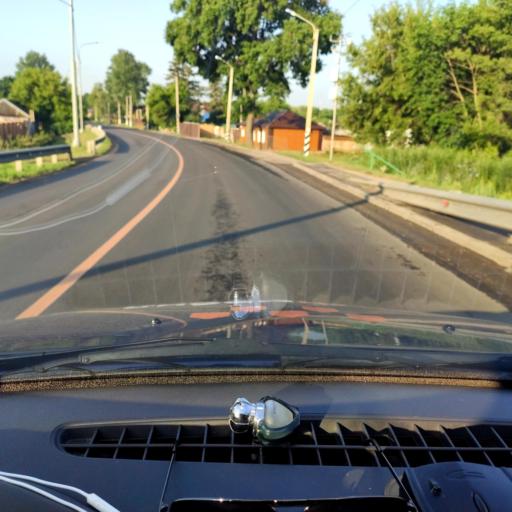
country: RU
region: Lipetsk
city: Izmalkovo
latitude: 52.4881
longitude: 38.0416
